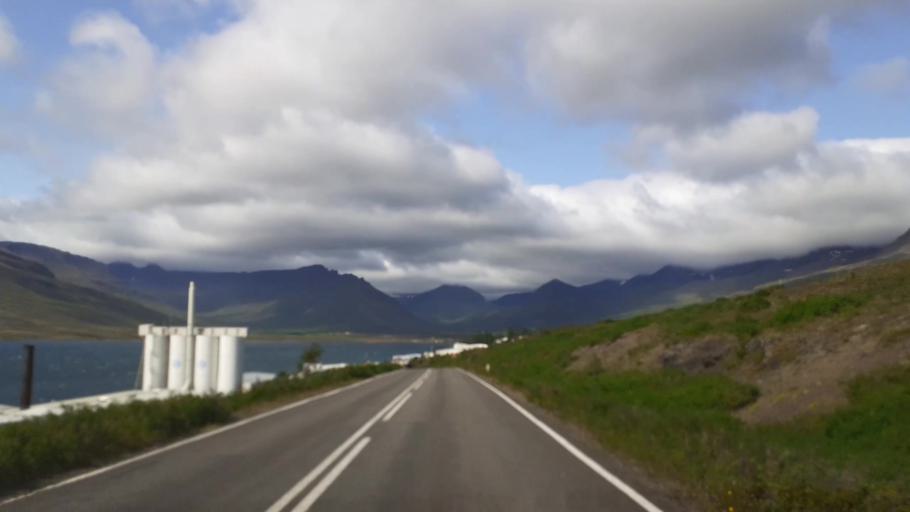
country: IS
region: East
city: Eskifjoerdur
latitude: 64.9242
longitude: -13.9858
